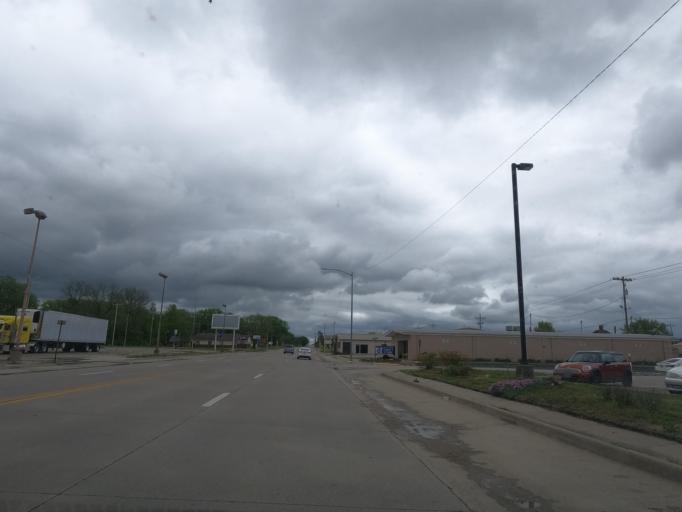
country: US
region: Kansas
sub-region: Labette County
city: Parsons
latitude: 37.3405
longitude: -95.2521
